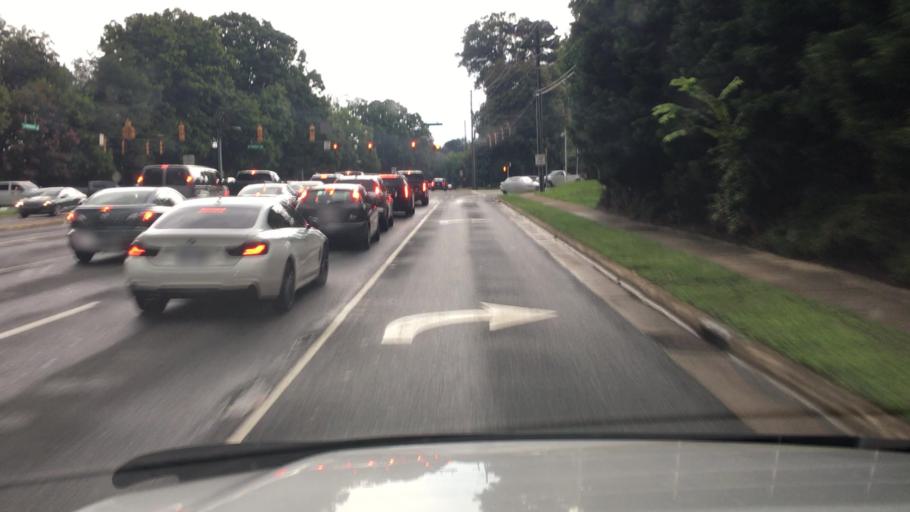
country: US
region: North Carolina
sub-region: Mecklenburg County
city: Matthews
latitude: 35.1550
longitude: -80.7956
